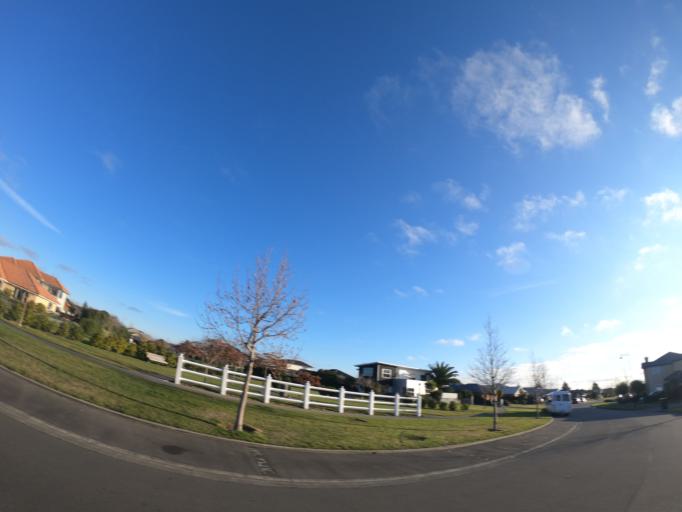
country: NZ
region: Canterbury
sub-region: Selwyn District
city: Prebbleton
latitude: -43.5669
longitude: 172.5667
